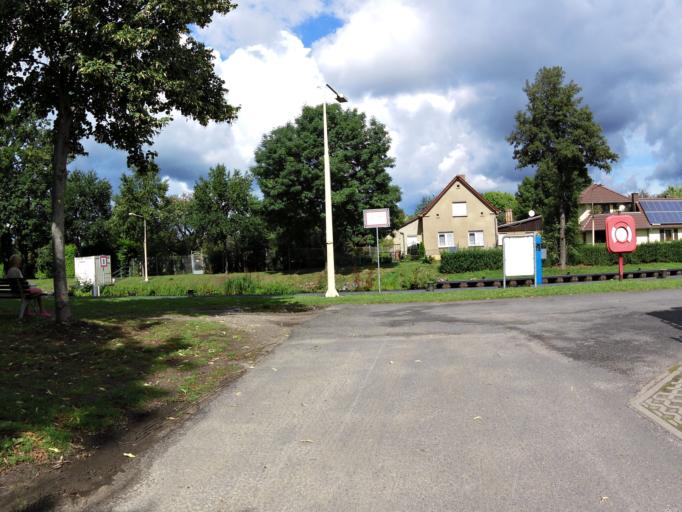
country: DE
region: Brandenburg
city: Storkow
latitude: 52.2581
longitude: 13.9316
